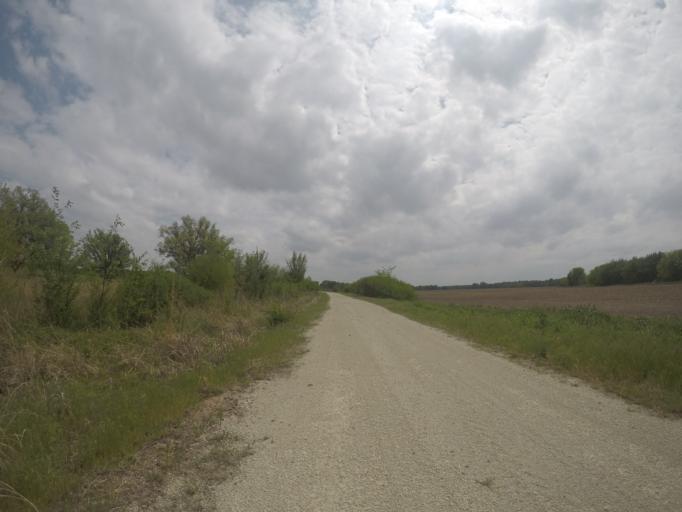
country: US
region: Nebraska
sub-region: Gage County
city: Wymore
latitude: 40.0112
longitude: -96.5944
